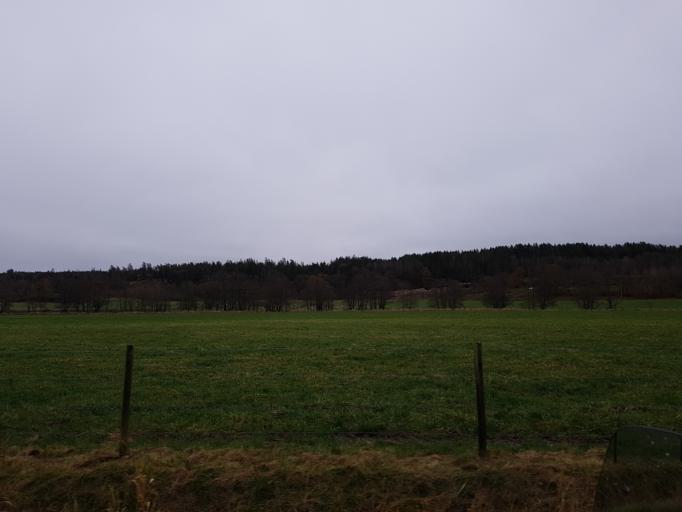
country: SE
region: Vaestra Goetaland
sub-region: Orust
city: Henan
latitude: 58.2535
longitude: 11.7512
